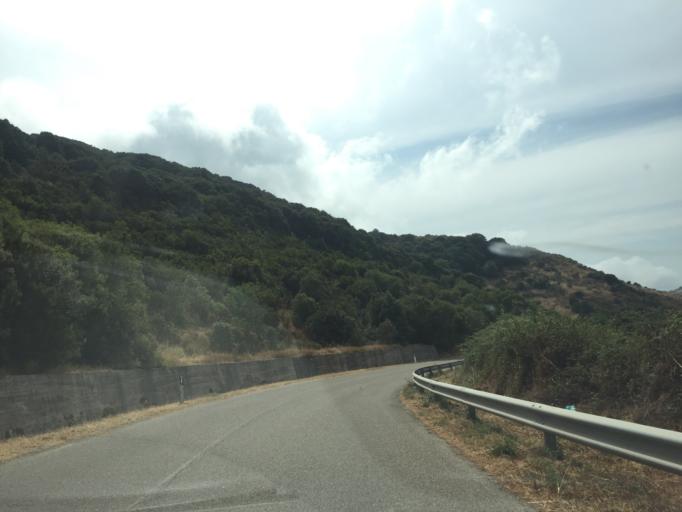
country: IT
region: Sardinia
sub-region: Provincia di Olbia-Tempio
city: Trinita d'Agultu
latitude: 40.9749
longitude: 8.9494
